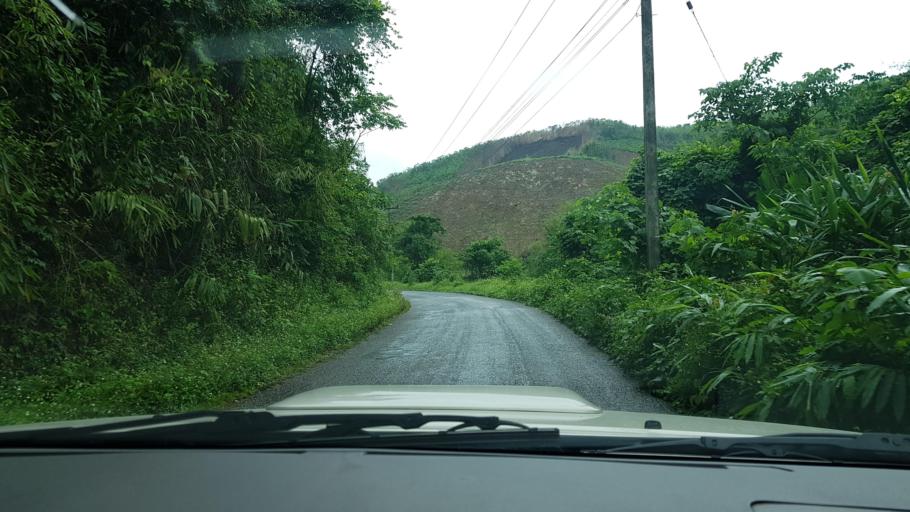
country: LA
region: Phongsali
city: Khoa
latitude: 21.1023
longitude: 102.2900
